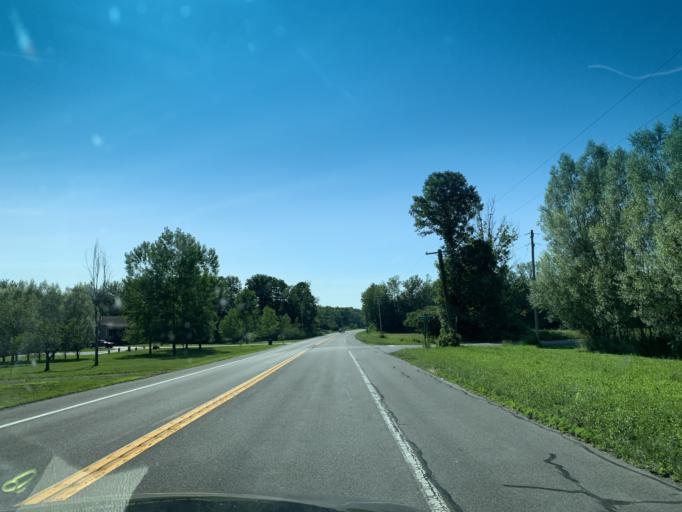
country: US
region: New York
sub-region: Madison County
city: Oneida
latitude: 43.1459
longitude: -75.6578
